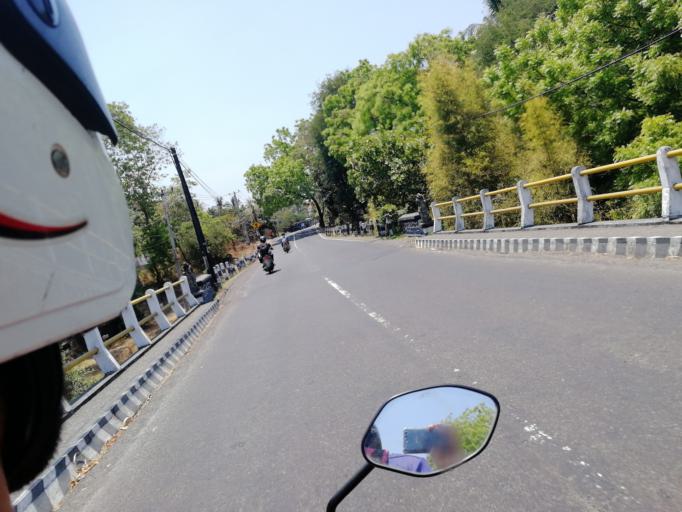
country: ID
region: Bali
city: Banjar Trunyan
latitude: -8.1529
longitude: 115.4165
